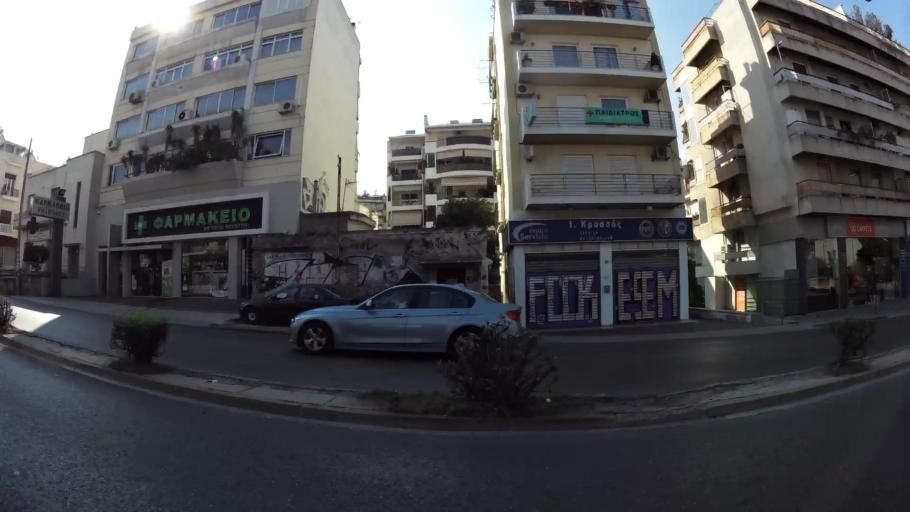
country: GR
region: Attica
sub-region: Nomarchia Athinas
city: Galatsi
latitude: 38.0157
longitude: 23.7421
